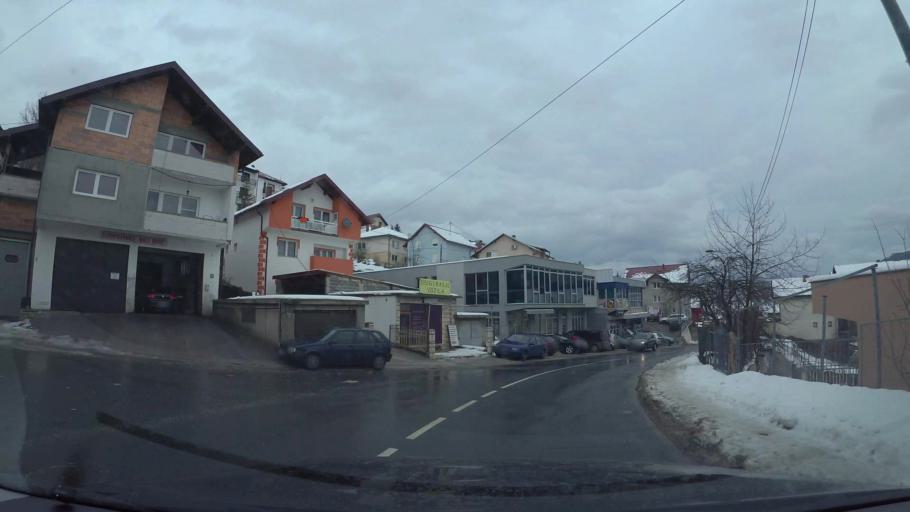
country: BA
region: Federation of Bosnia and Herzegovina
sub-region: Kanton Sarajevo
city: Sarajevo
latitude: 43.8620
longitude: 18.3585
